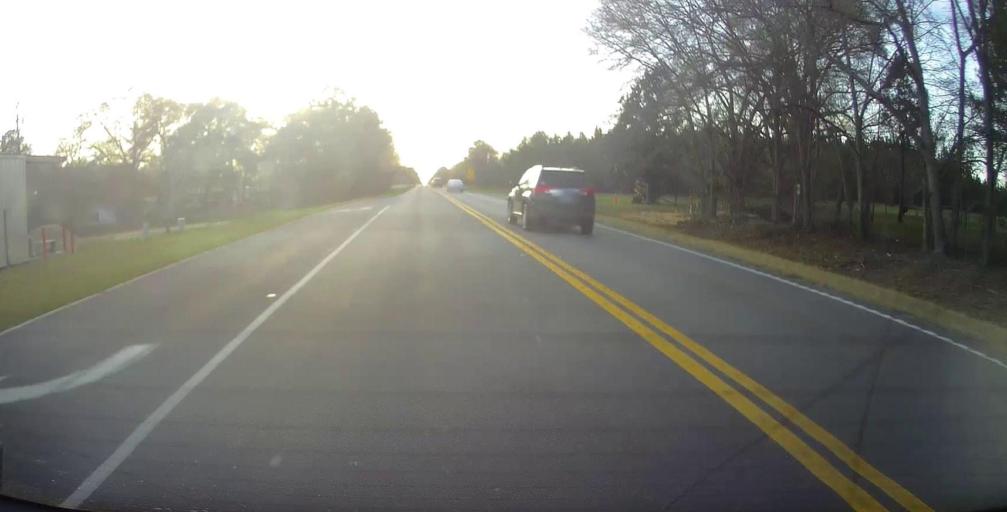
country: US
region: Georgia
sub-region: Evans County
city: Claxton
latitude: 32.1525
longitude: -81.8195
